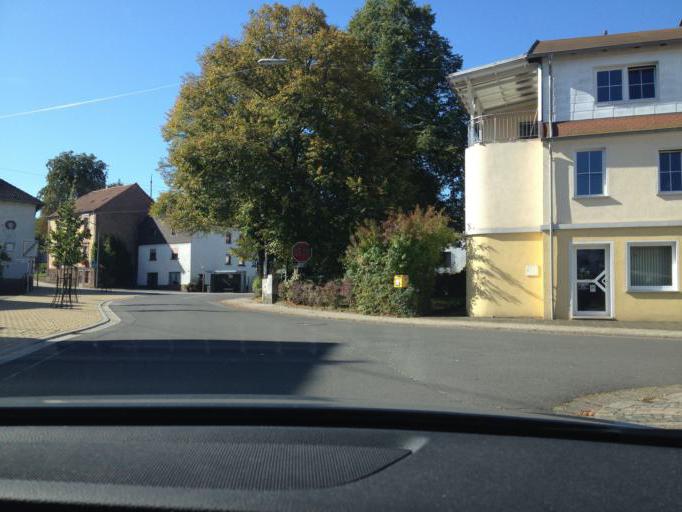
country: DE
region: Saarland
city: Marpingen
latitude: 49.4323
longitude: 7.0758
